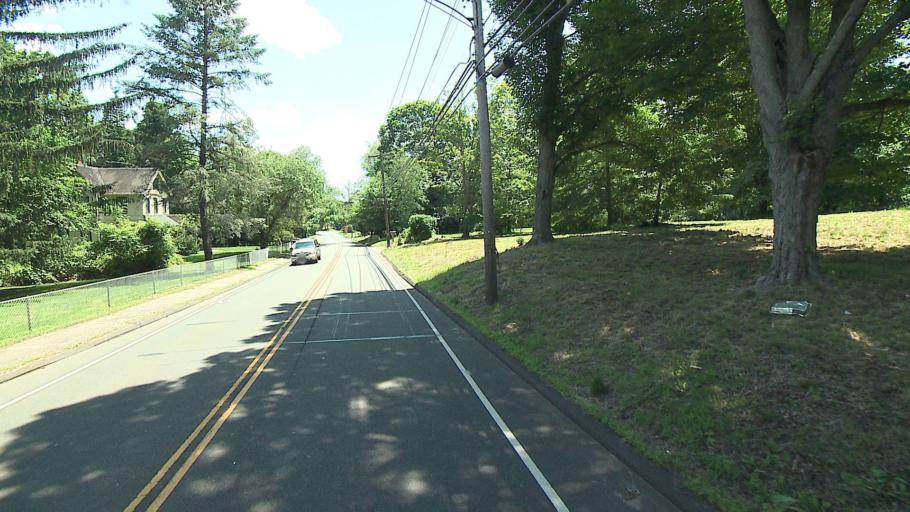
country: US
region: Connecticut
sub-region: Fairfield County
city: Trumbull
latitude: 41.2501
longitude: -73.1973
